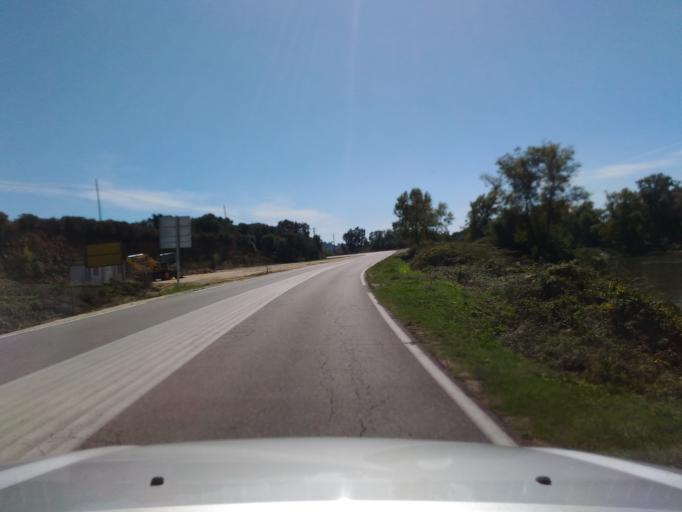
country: FR
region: Corsica
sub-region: Departement de la Haute-Corse
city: Aleria
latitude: 42.1176
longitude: 9.4912
